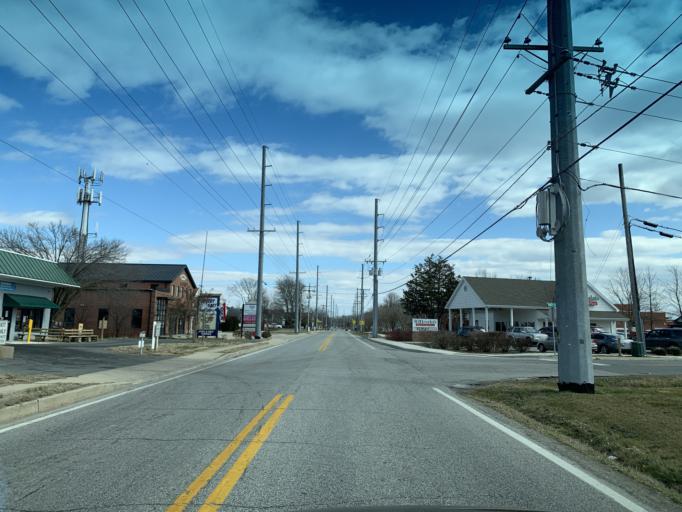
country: US
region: Maryland
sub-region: Queen Anne's County
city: Stevensville
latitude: 38.9787
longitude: -76.3107
